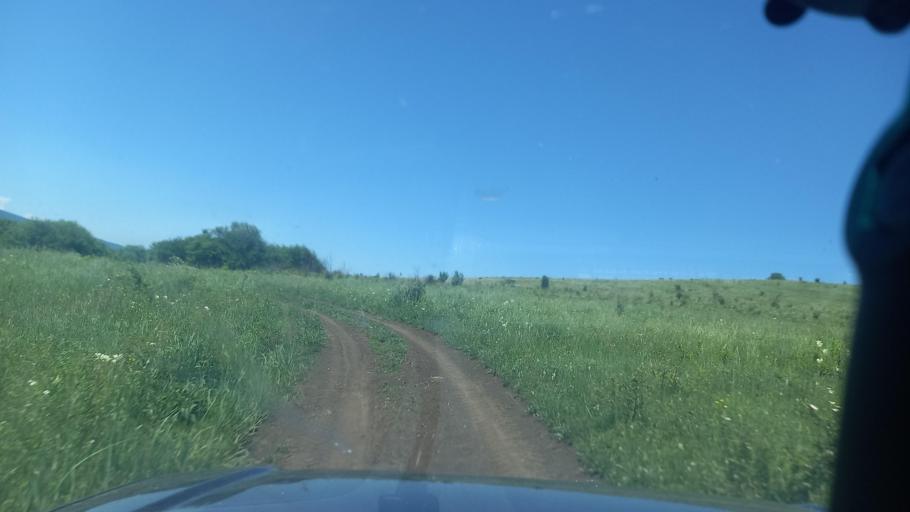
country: RU
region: Karachayevo-Cherkesiya
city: Pregradnaya
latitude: 44.1047
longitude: 41.1343
